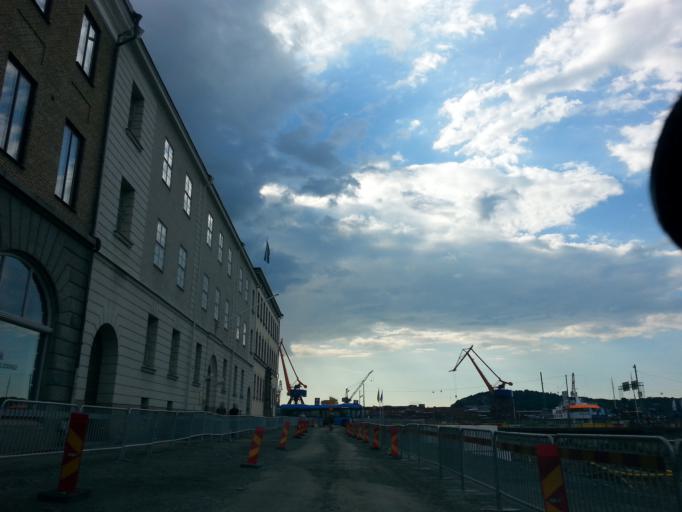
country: SE
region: Vaestra Goetaland
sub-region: Goteborg
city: Goeteborg
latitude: 57.7059
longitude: 11.9609
